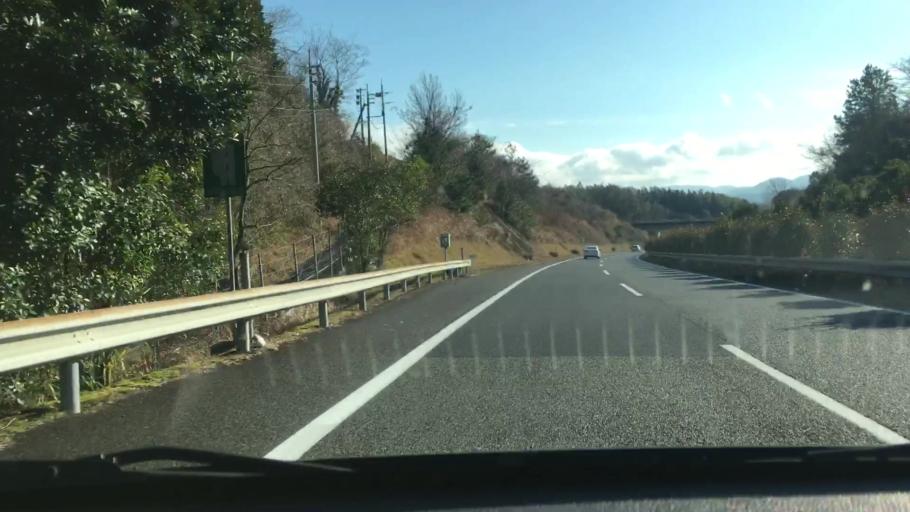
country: JP
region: Kumamoto
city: Hitoyoshi
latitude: 32.2210
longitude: 130.7802
